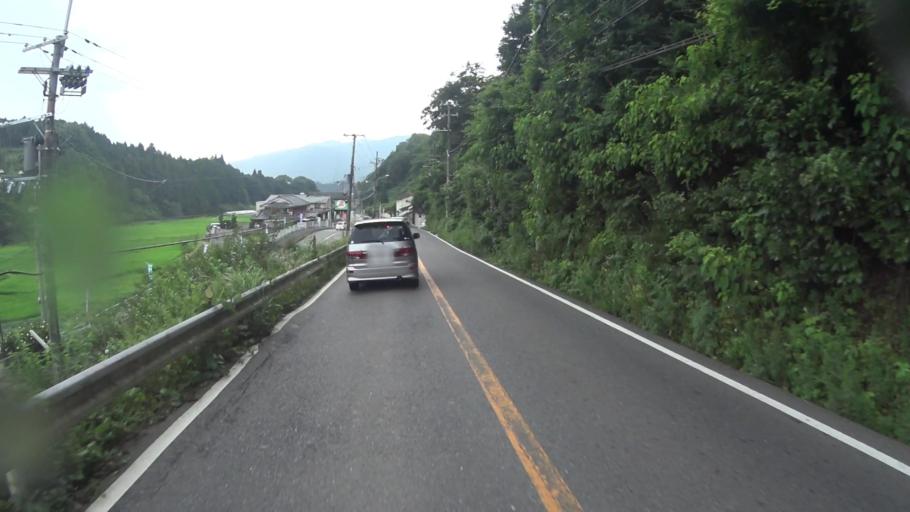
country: JP
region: Kyoto
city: Uji
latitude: 34.8564
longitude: 135.8954
